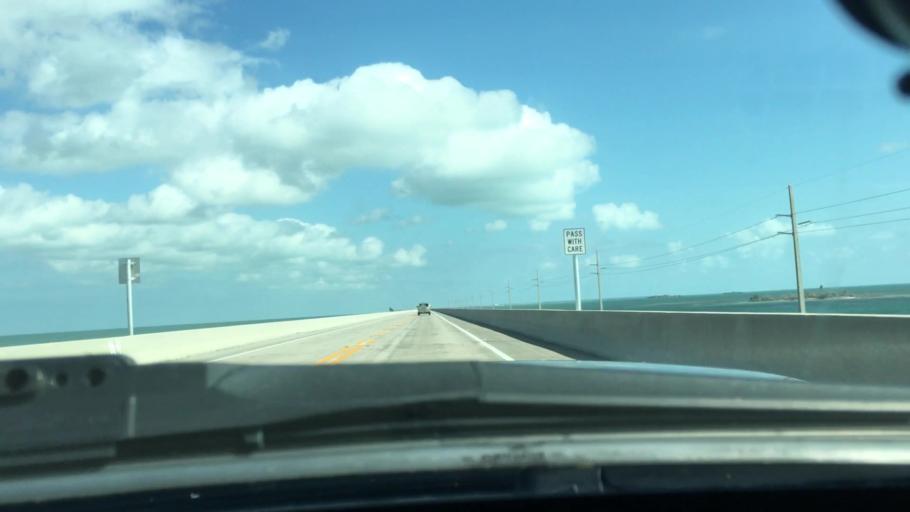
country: US
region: Florida
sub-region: Monroe County
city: Big Pine Key
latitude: 24.6841
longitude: -81.2219
